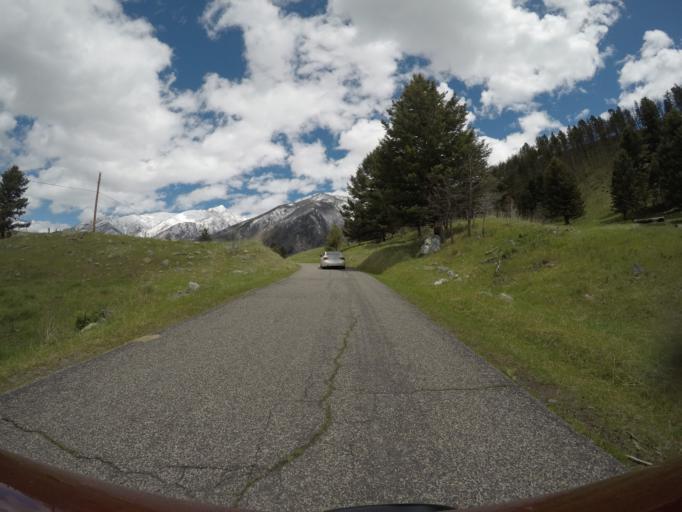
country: US
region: Montana
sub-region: Park County
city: Livingston
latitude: 45.4997
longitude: -110.5442
